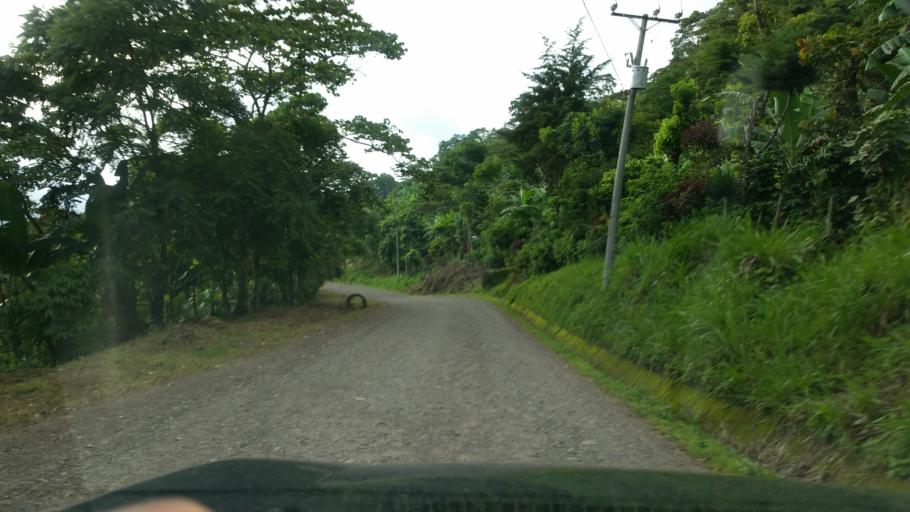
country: NI
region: Jinotega
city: Jinotega
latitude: 13.2422
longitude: -85.7277
